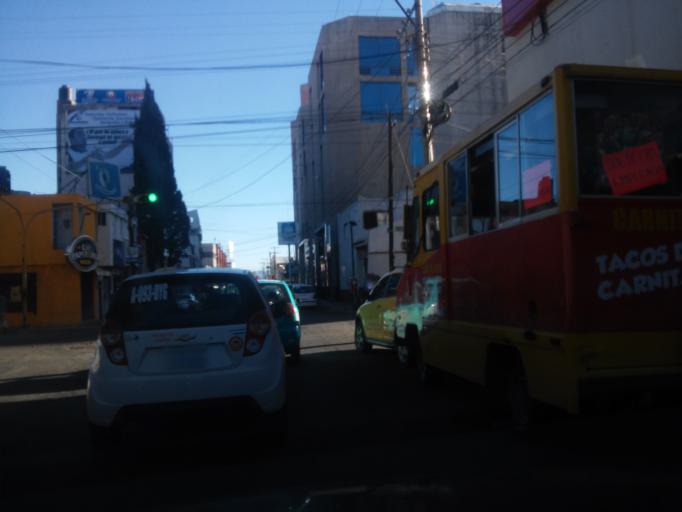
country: MX
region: Durango
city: Victoria de Durango
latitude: 24.0308
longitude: -104.6478
